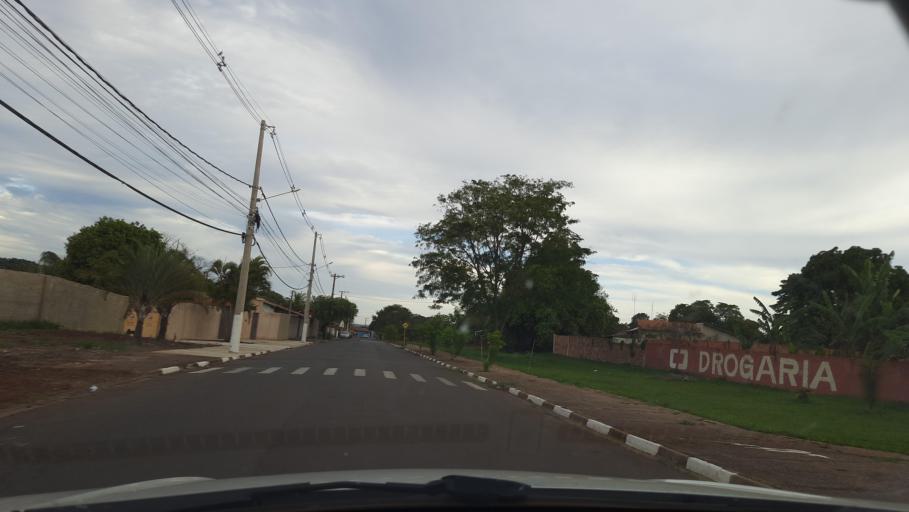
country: BR
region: Sao Paulo
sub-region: Casa Branca
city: Casa Branca
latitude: -21.7787
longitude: -47.0689
